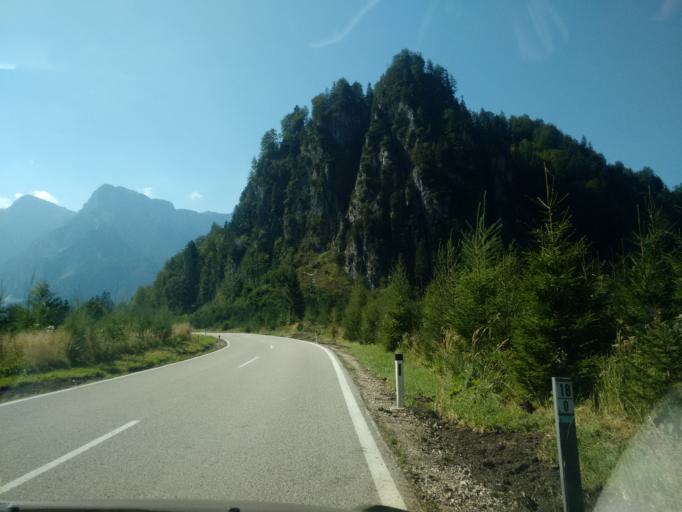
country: AT
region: Upper Austria
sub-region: Politischer Bezirk Gmunden
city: Gruenau im Almtal
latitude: 47.7619
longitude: 13.9540
